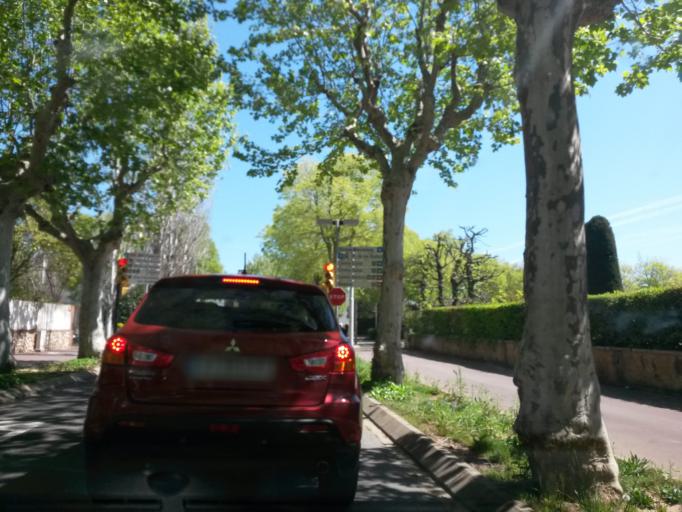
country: ES
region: Catalonia
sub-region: Provincia de Girona
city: Banyoles
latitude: 42.1159
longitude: 2.7572
